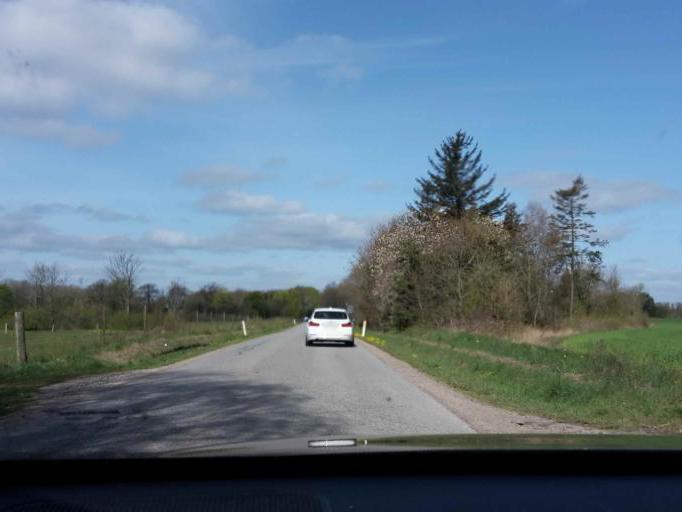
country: DK
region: South Denmark
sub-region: Vejen Kommune
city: Holsted
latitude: 55.5858
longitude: 8.9603
